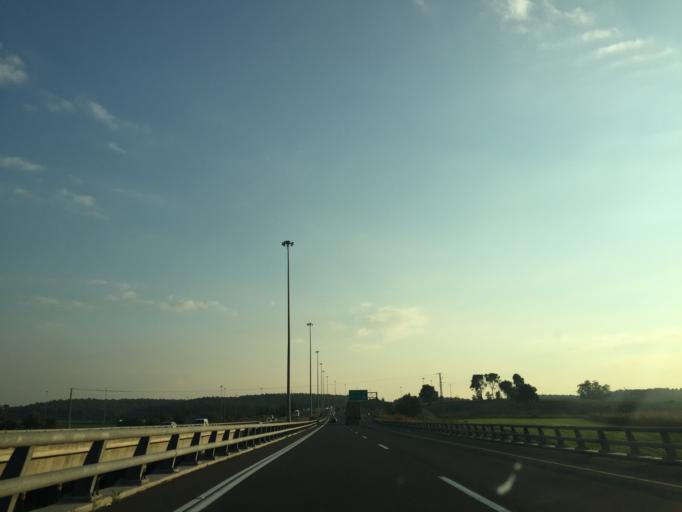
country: IL
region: Southern District
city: Qiryat Gat
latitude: 31.6063
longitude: 34.8135
